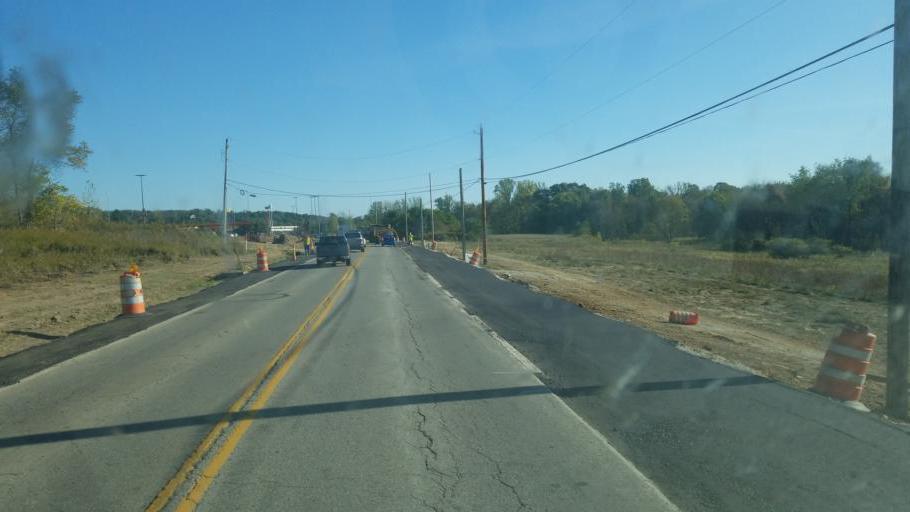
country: US
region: Ohio
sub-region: Richland County
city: Lexington
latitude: 40.6557
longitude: -82.5487
